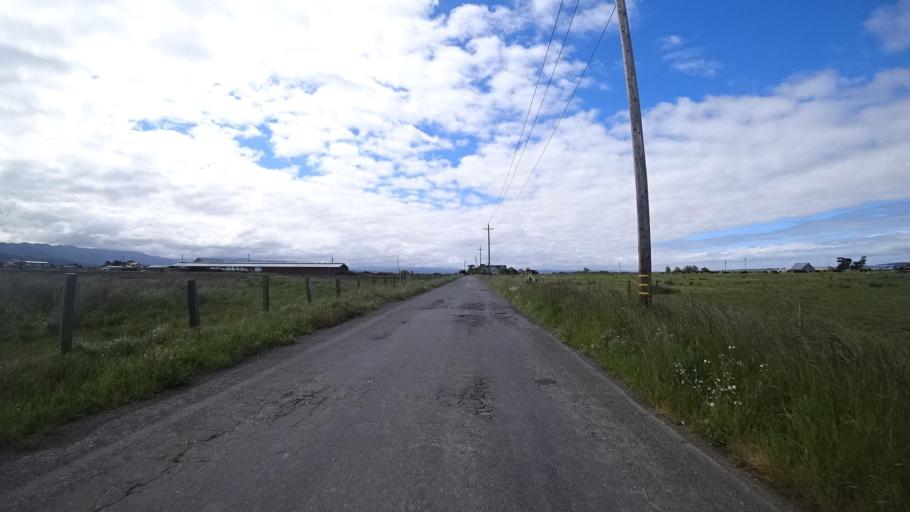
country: US
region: California
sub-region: Humboldt County
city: Arcata
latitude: 40.8854
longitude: -124.1157
